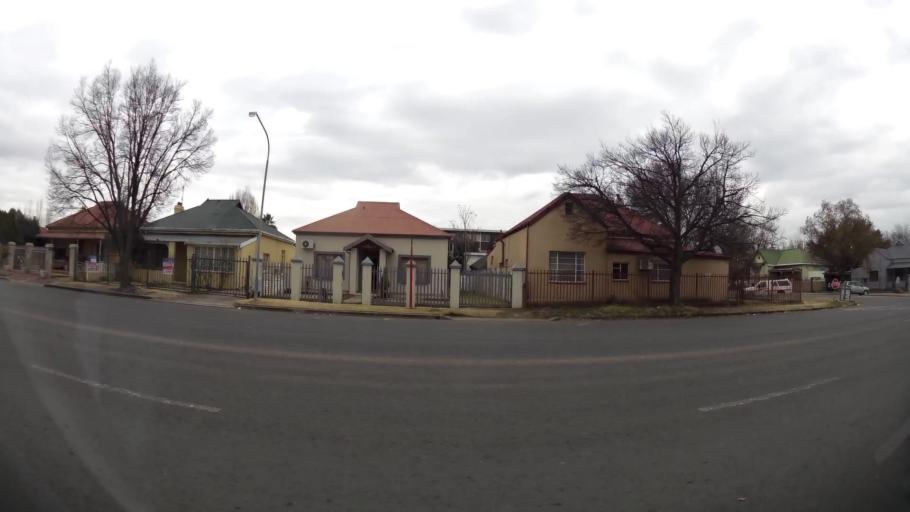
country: ZA
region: Orange Free State
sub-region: Fezile Dabi District Municipality
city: Kroonstad
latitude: -27.6610
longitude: 27.2410
